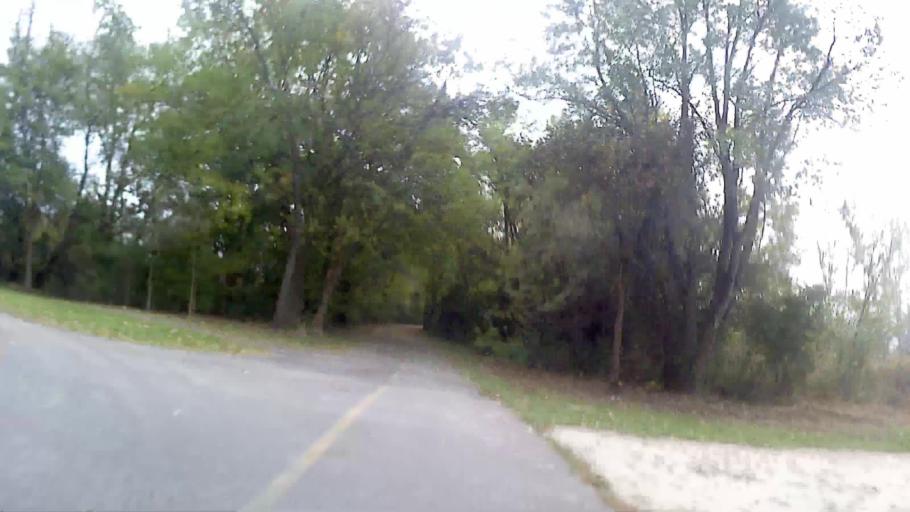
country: US
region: Illinois
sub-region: Kane County
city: Montgomery
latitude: 41.7582
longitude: -88.3854
